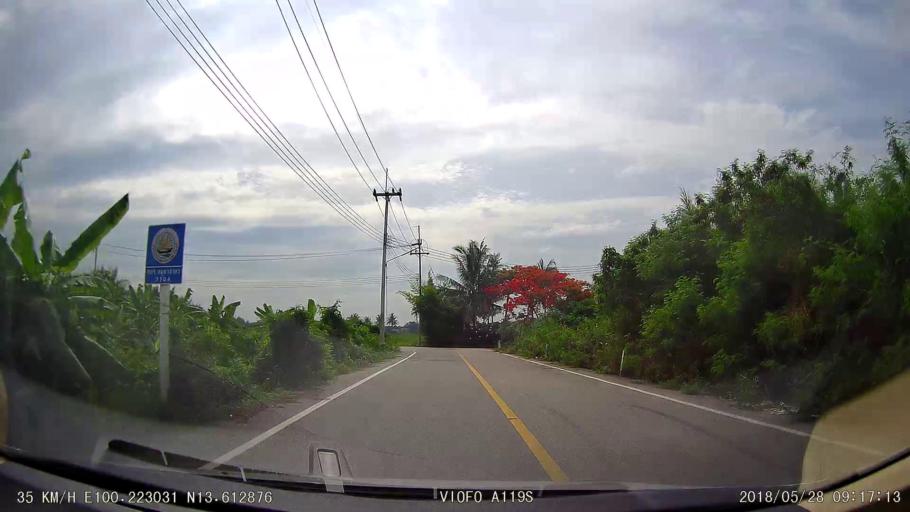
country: TH
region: Samut Sakhon
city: Krathum Baen
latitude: 13.6153
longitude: 100.2239
